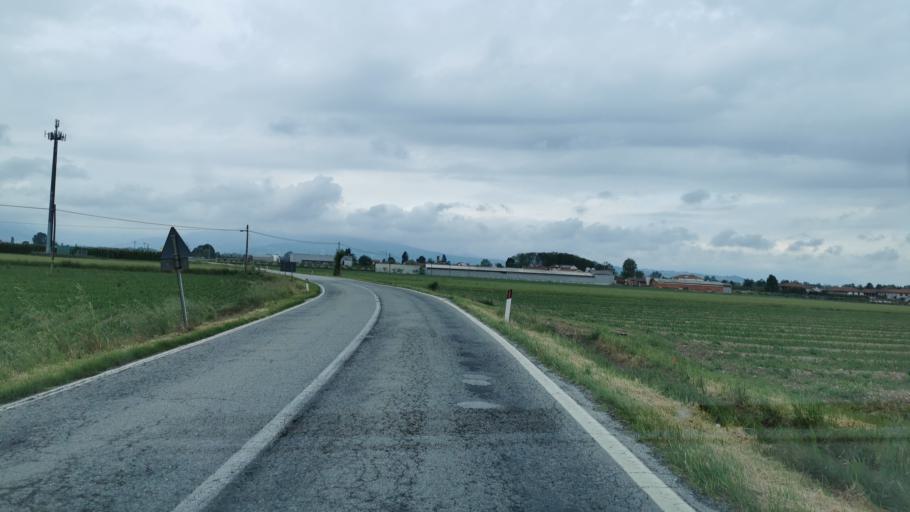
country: IT
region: Piedmont
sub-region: Provincia di Cuneo
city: Lagnasco
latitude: 44.6063
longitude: 7.5877
